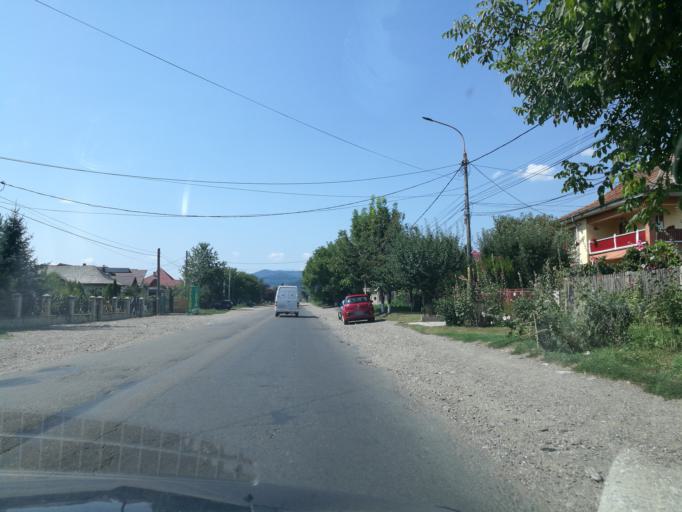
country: RO
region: Neamt
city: Piatra Neamt
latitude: 46.9403
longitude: 26.3223
